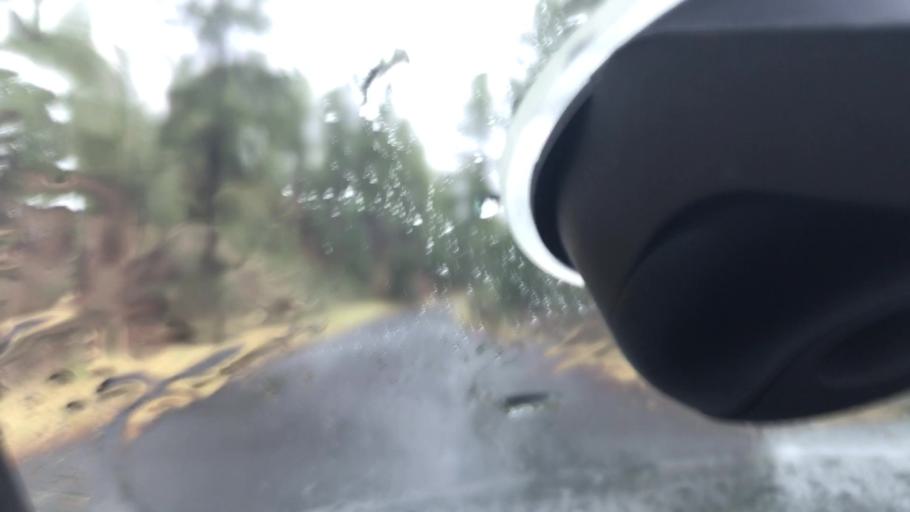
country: US
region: Arizona
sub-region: Yavapai County
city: Prescott
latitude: 34.5087
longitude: -112.3824
